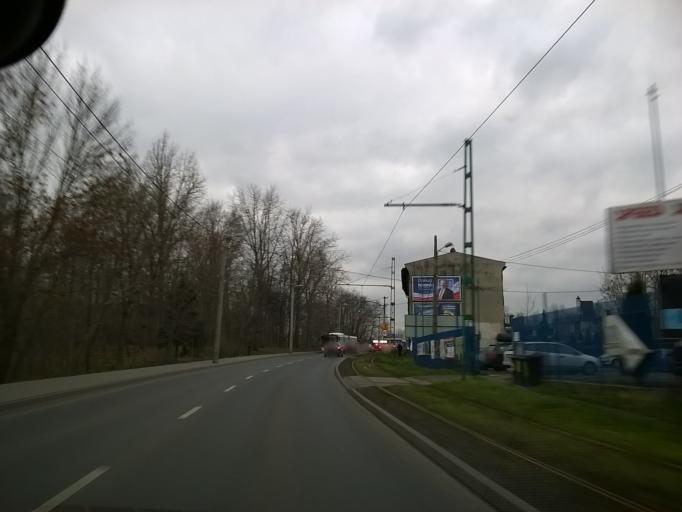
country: PL
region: Silesian Voivodeship
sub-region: Swietochlowice
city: Swietochlowice
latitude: 50.2787
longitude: 18.9116
